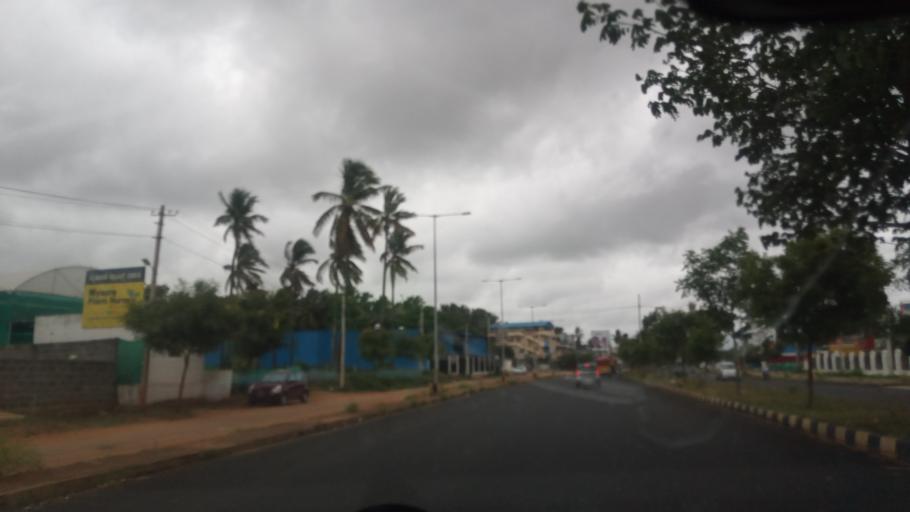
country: IN
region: Karnataka
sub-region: Mysore
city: Mysore
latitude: 12.3024
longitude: 76.6022
